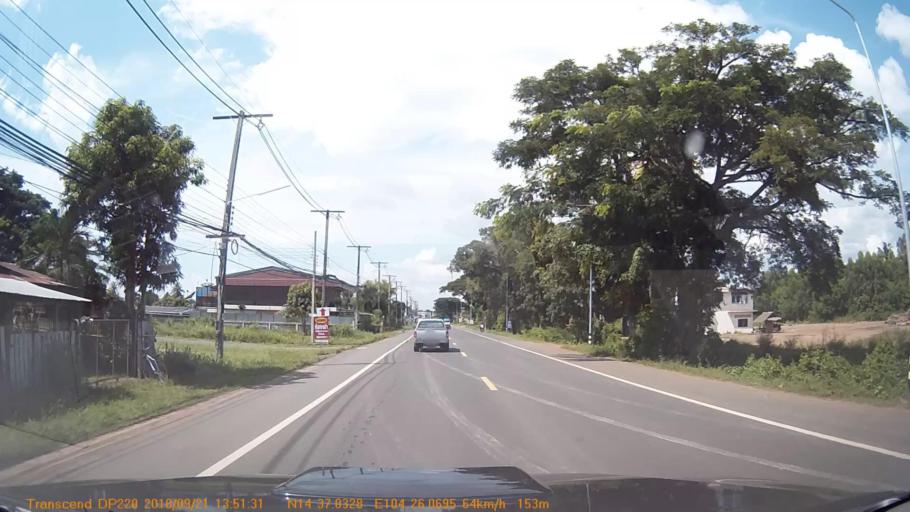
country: TH
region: Sisaket
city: Khun Han
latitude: 14.6175
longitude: 104.4345
